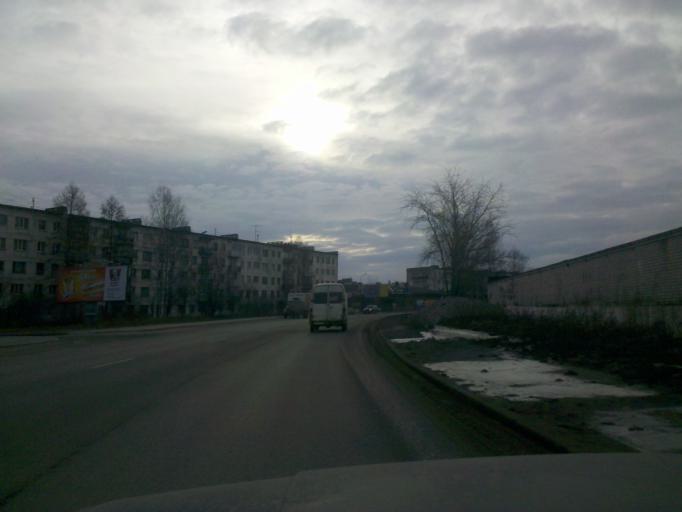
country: RU
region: Republic of Karelia
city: Petrozavodsk
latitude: 61.7946
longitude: 34.3363
